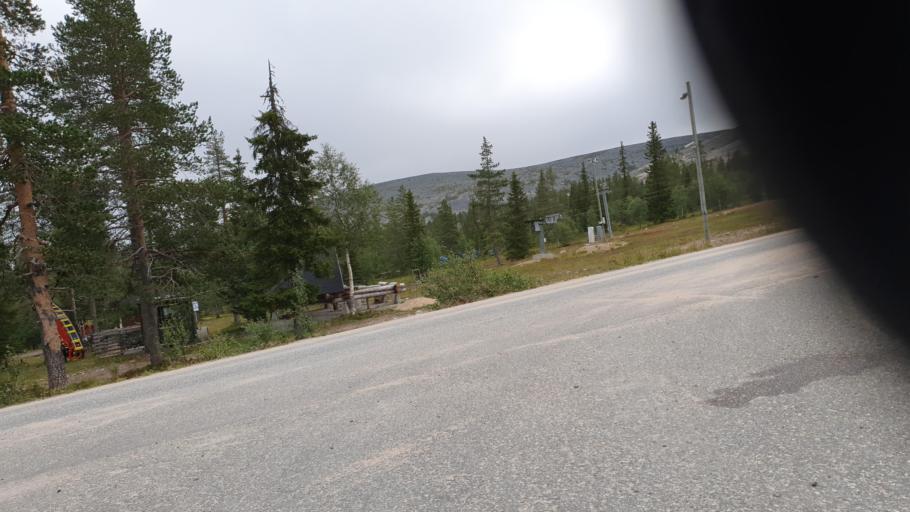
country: FI
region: Lapland
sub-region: Tunturi-Lappi
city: Kolari
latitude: 67.5830
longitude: 24.2053
